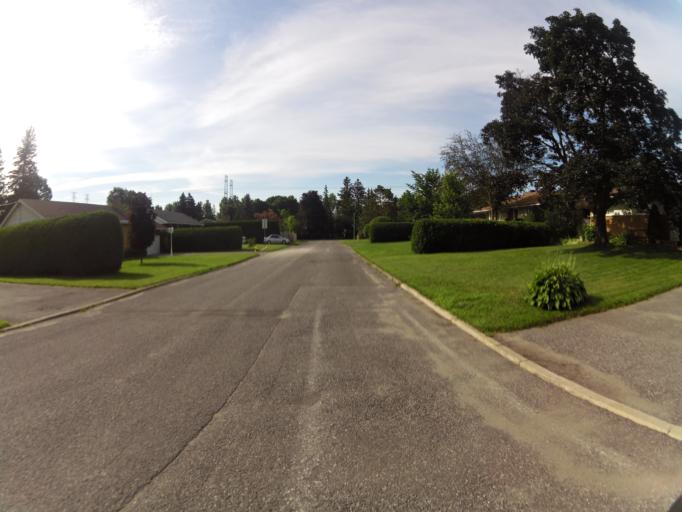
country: CA
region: Ontario
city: Bells Corners
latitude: 45.3261
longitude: -75.7668
